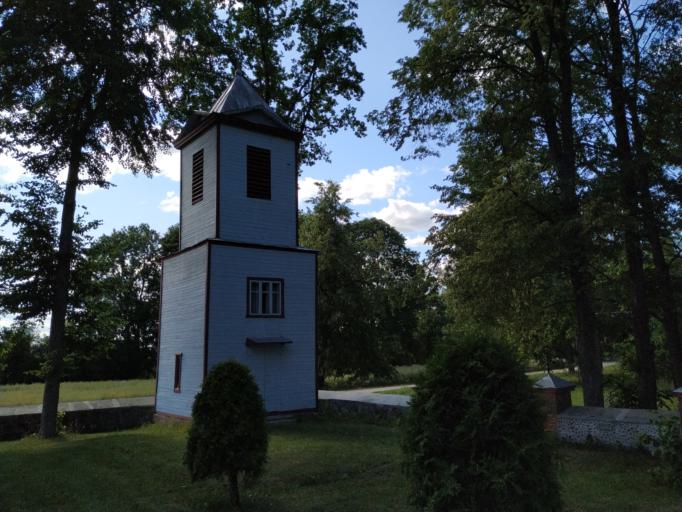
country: LT
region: Panevezys
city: Pasvalys
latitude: 56.1280
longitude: 24.3237
